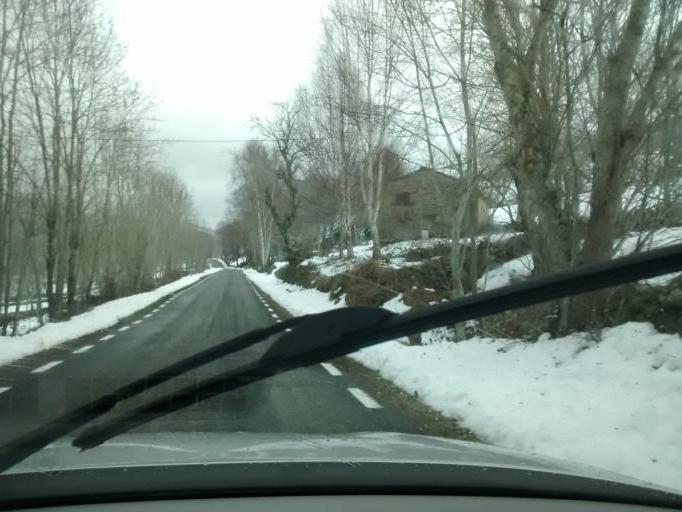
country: ES
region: Castille and Leon
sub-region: Provincia de Burgos
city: Espinosa de los Monteros
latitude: 43.1195
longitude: -3.6584
